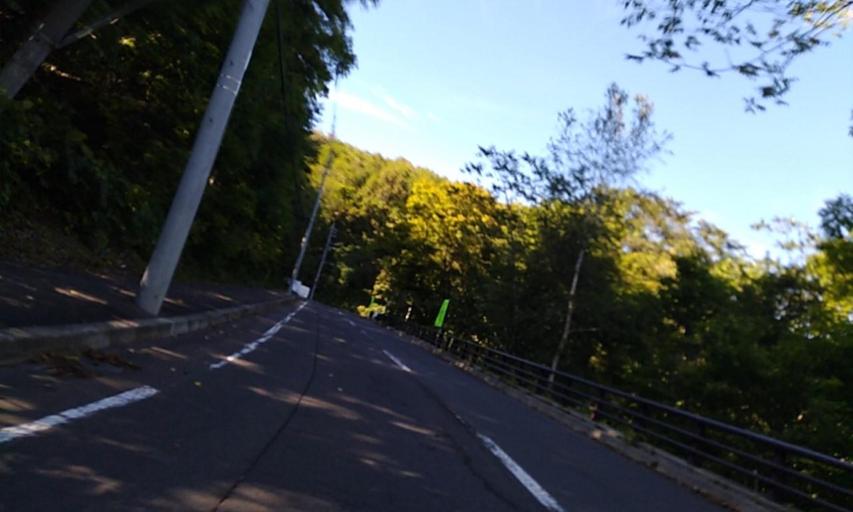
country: JP
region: Hokkaido
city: Sapporo
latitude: 43.0495
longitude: 141.2921
